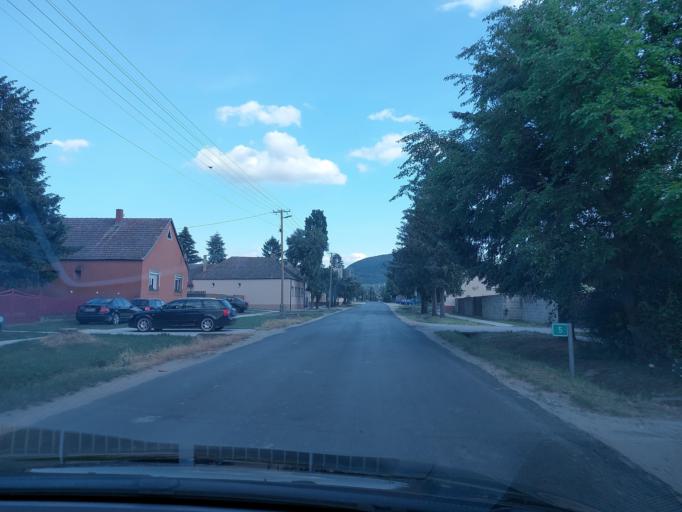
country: HU
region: Veszprem
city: Devecser
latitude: 47.1703
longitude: 17.3596
